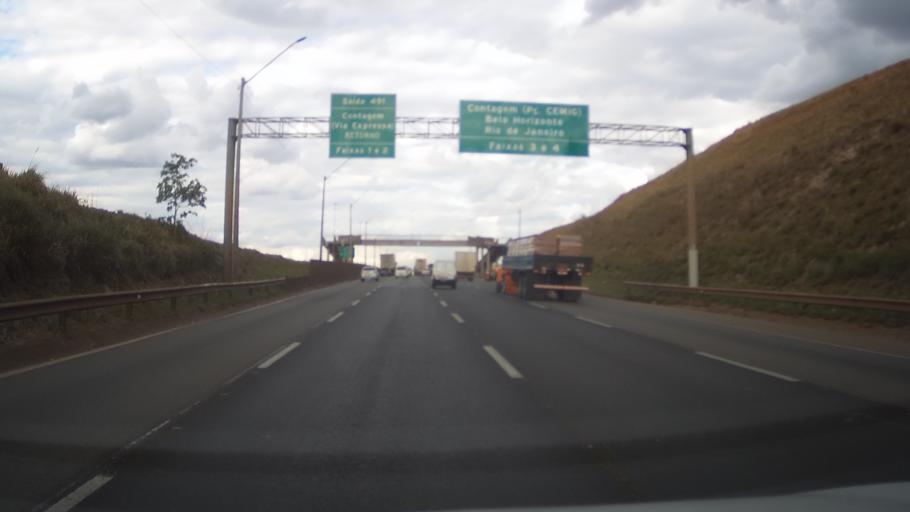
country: BR
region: Minas Gerais
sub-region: Betim
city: Betim
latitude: -19.9596
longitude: -44.1526
